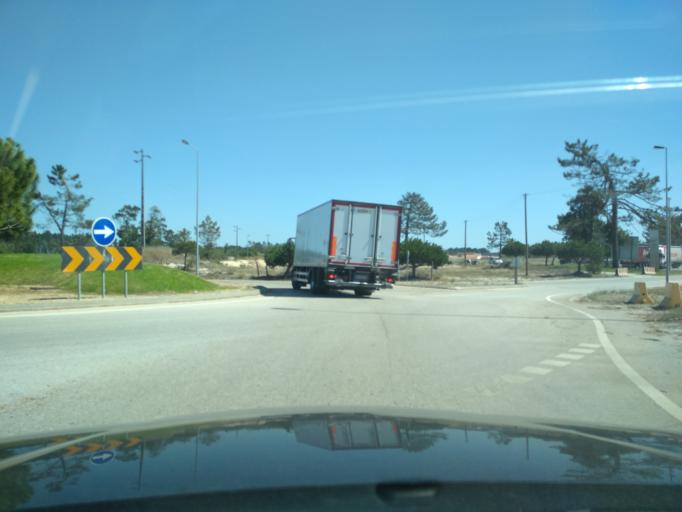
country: PT
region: Coimbra
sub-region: Figueira da Foz
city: Lavos
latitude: 40.0541
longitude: -8.8713
